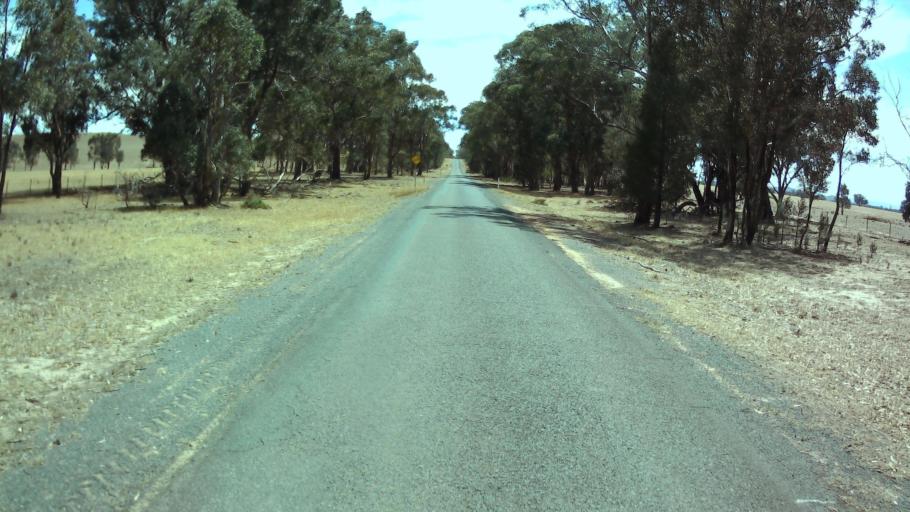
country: AU
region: New South Wales
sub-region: Weddin
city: Grenfell
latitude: -33.7644
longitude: 148.2045
